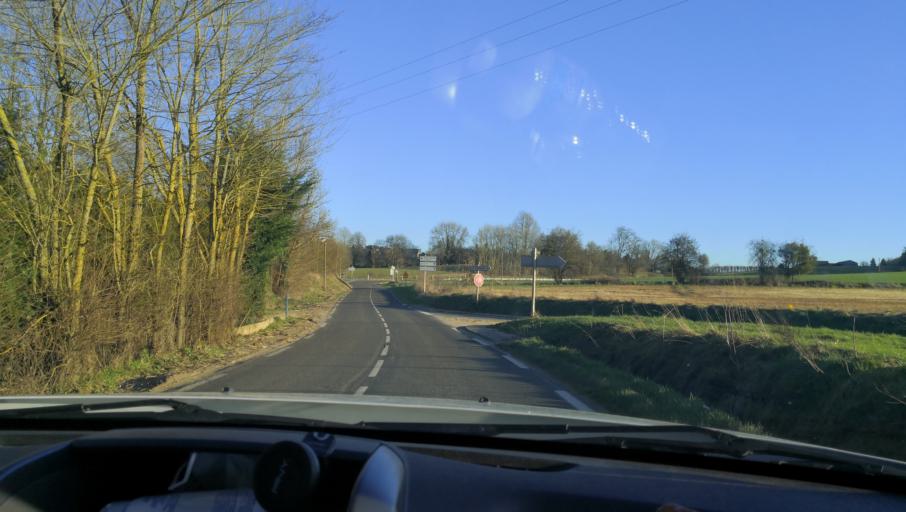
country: FR
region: Haute-Normandie
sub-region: Departement de la Seine-Maritime
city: Saint-Martin-Osmonville
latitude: 49.6132
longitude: 1.3256
